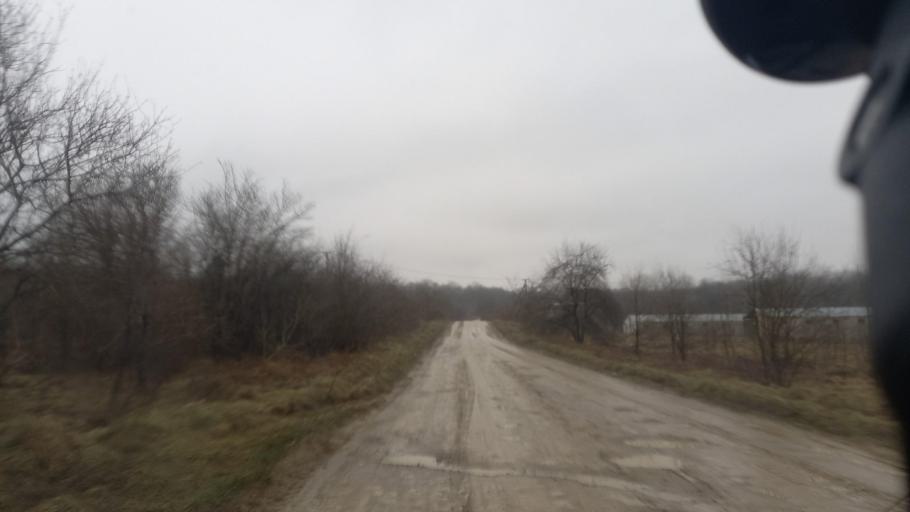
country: RU
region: Krasnodarskiy
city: Saratovskaya
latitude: 44.6662
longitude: 39.2169
